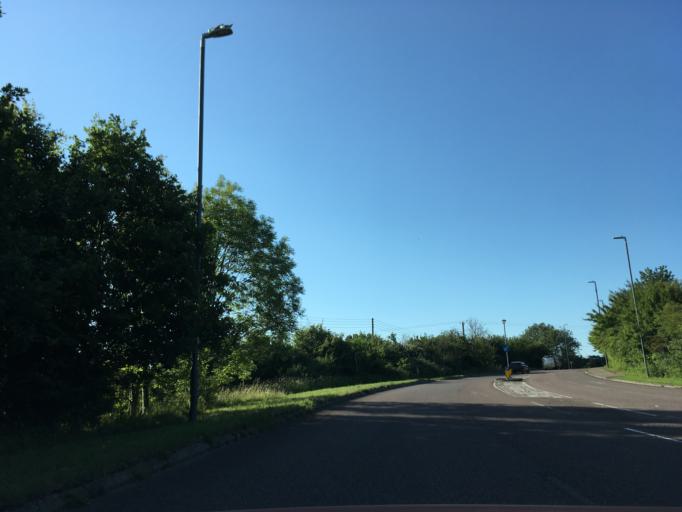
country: GB
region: England
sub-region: South Gloucestershire
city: Siston
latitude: 51.4699
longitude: -2.4783
